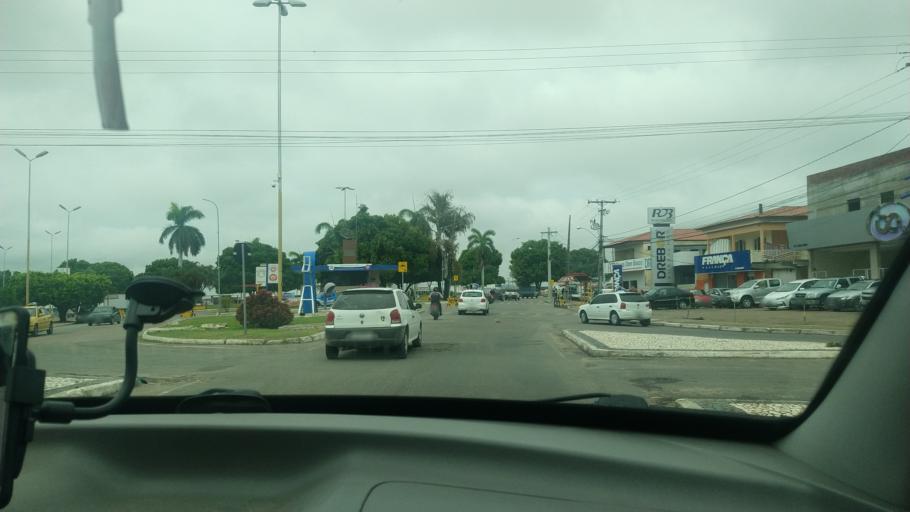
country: BR
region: Bahia
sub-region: Paulo Afonso
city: Paulo Afonso
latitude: -9.4012
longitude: -38.2366
